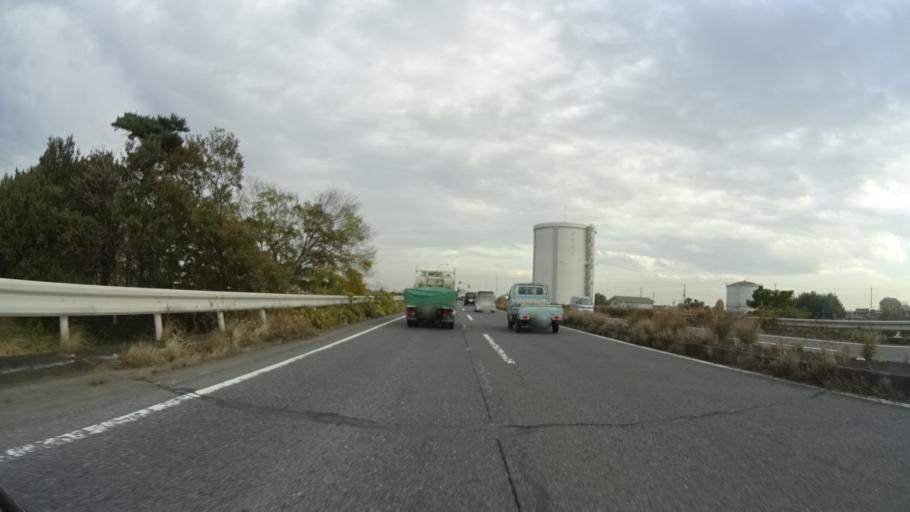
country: JP
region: Gunma
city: Isesaki
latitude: 36.3620
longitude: 139.1905
